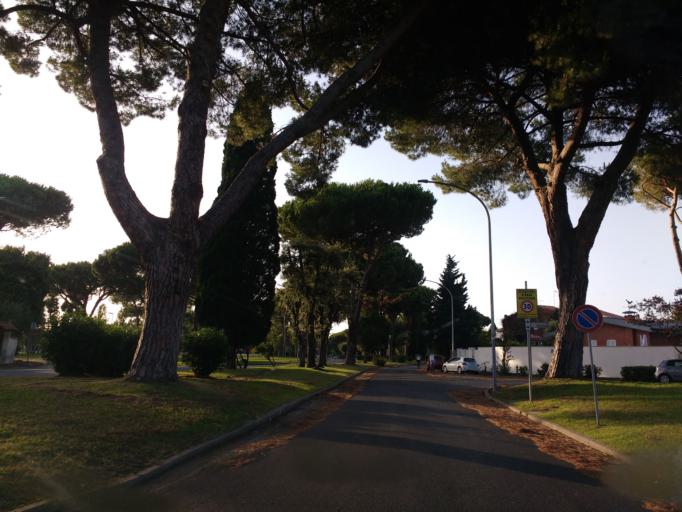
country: IT
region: Latium
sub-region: Citta metropolitana di Roma Capitale
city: Acilia-Castel Fusano-Ostia Antica
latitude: 41.7541
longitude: 12.3624
